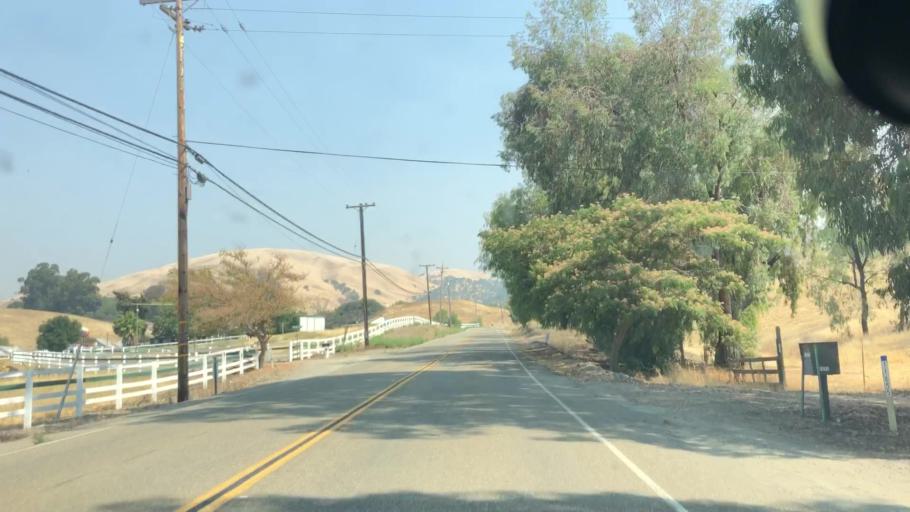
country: US
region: California
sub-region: Alameda County
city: Livermore
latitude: 37.6469
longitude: -121.6494
